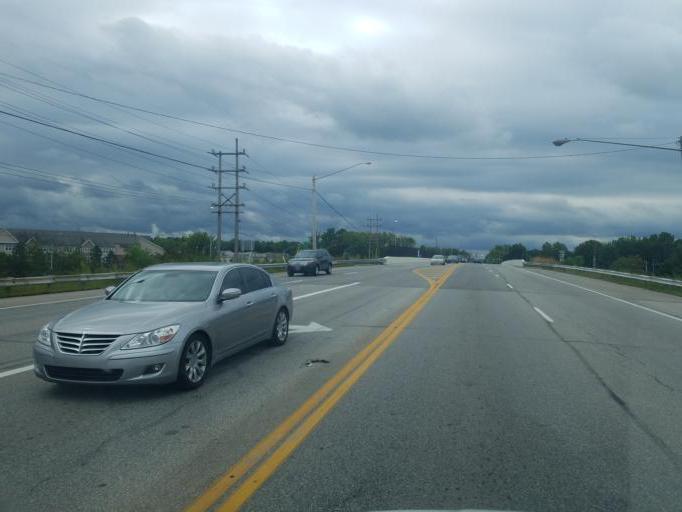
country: US
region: Ohio
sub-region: Lake County
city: Fairport Harbor
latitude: 41.7189
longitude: -81.2984
